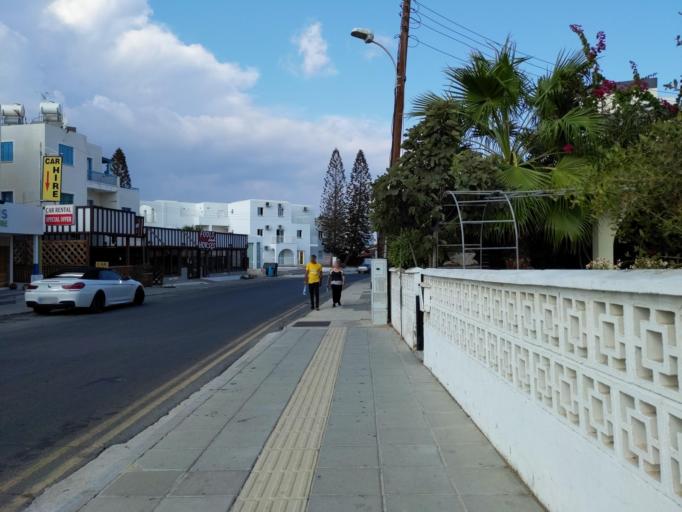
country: CY
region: Ammochostos
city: Protaras
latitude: 35.0272
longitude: 34.0413
